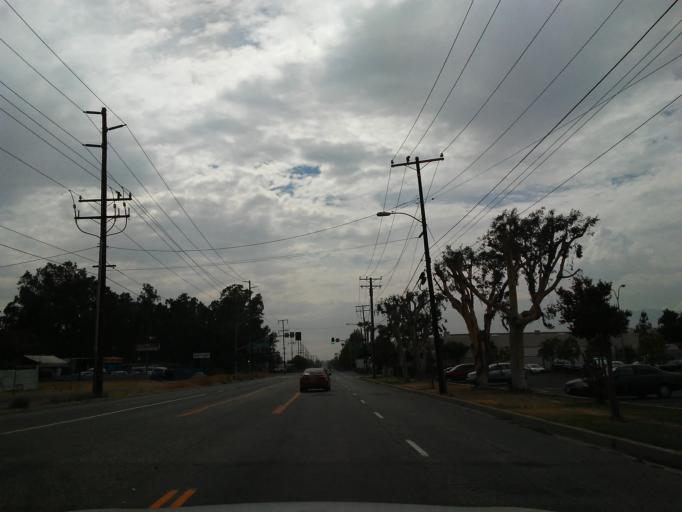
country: US
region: California
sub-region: San Bernardino County
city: San Bernardino
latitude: 34.0922
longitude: -117.2714
